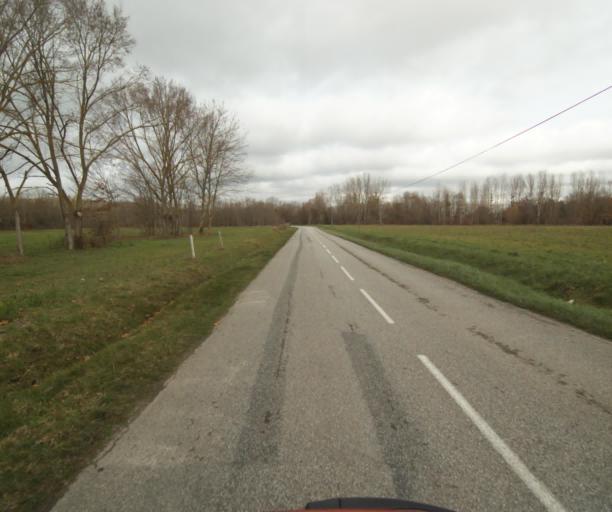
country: FR
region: Midi-Pyrenees
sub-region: Departement de l'Ariege
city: Pamiers
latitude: 43.1391
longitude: 1.5949
